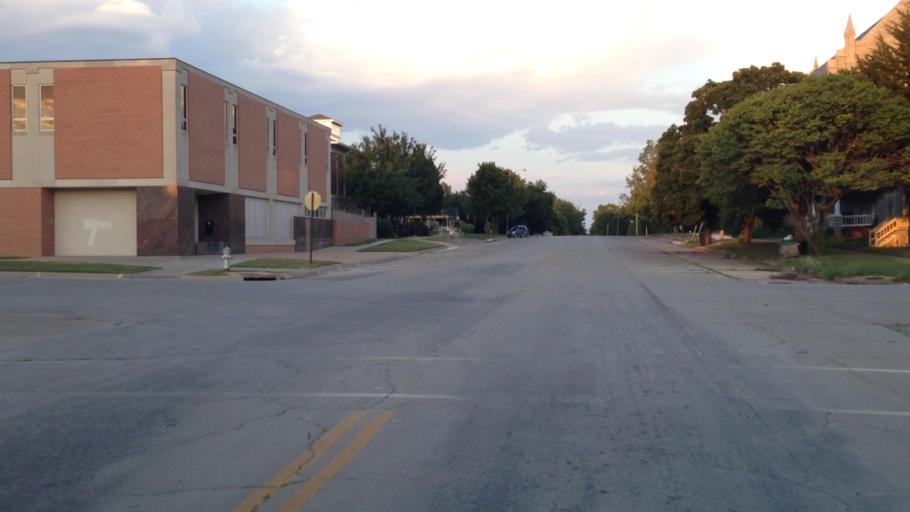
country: US
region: Kansas
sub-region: Montgomery County
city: Independence
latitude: 37.2221
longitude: -95.7056
